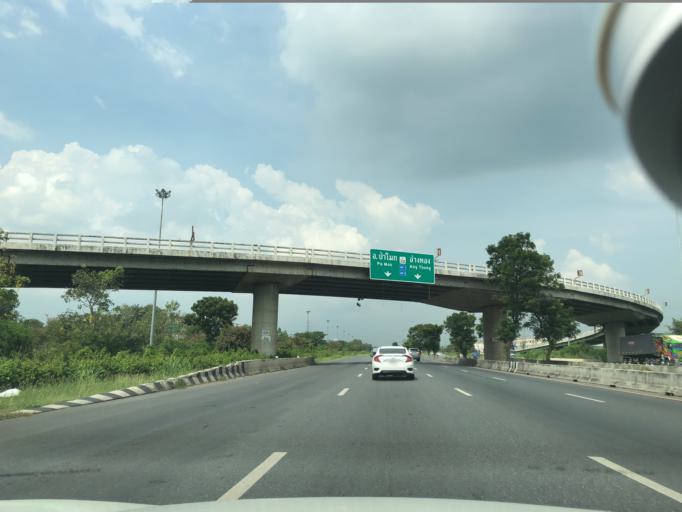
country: TH
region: Phra Nakhon Si Ayutthaya
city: Bang Pahan
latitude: 14.4494
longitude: 100.5406
